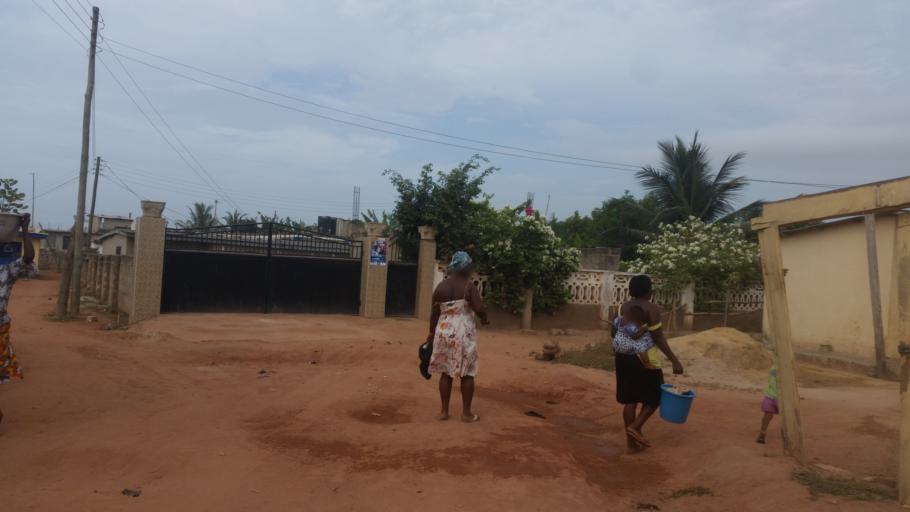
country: GH
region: Central
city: Cape Coast
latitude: 5.1238
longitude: -1.3038
